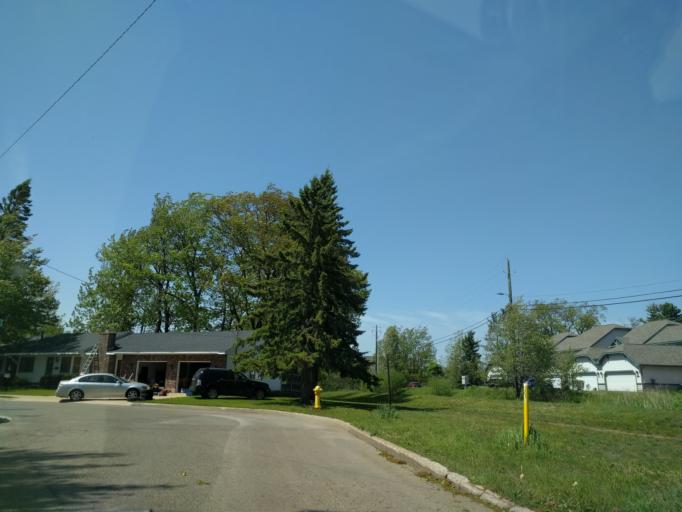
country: US
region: Michigan
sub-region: Marquette County
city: Marquette
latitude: 46.5545
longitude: -87.3866
